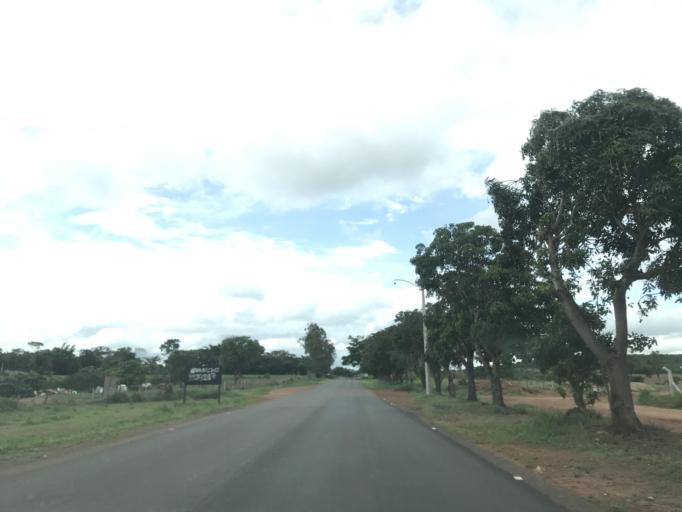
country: BR
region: Goias
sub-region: Bela Vista De Goias
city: Bela Vista de Goias
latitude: -17.0466
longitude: -48.6643
